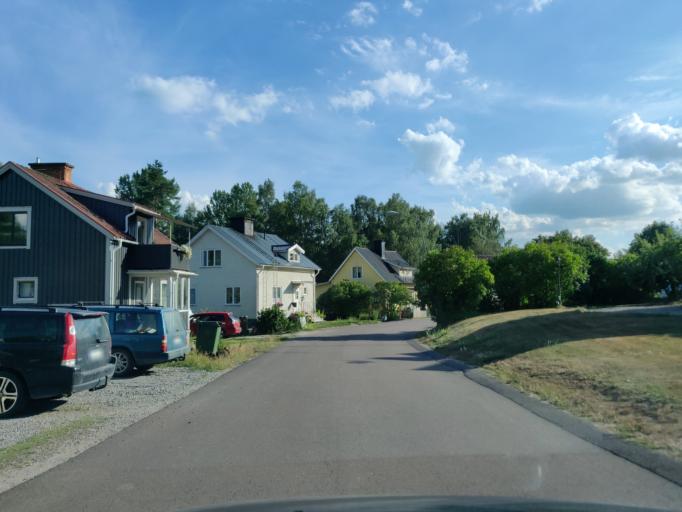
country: SE
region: Vaermland
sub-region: Hagfors Kommun
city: Hagfors
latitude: 60.0287
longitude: 13.7035
